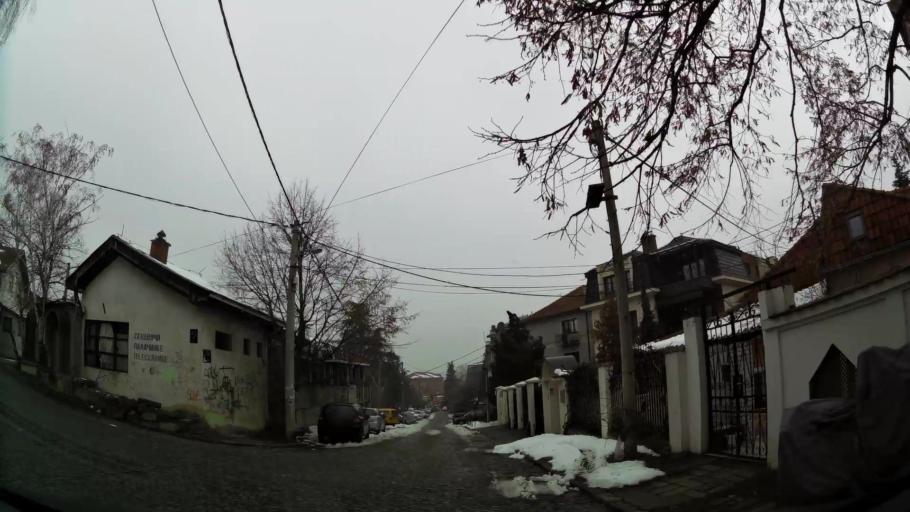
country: RS
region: Central Serbia
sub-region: Belgrade
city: Vozdovac
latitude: 44.7811
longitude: 20.4765
